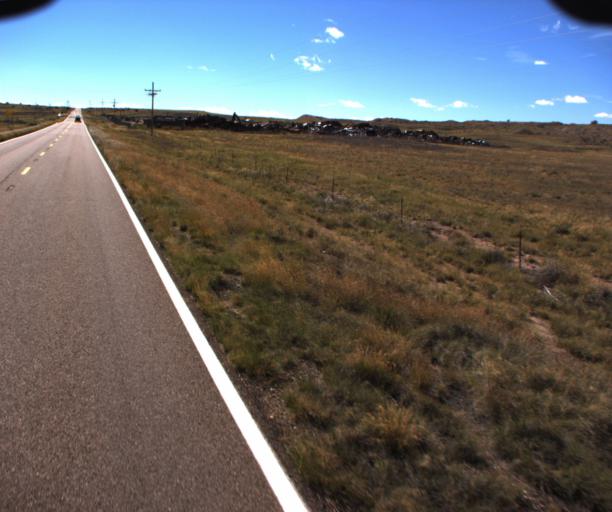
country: US
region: Arizona
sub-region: Apache County
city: Saint Johns
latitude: 34.5762
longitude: -109.3351
